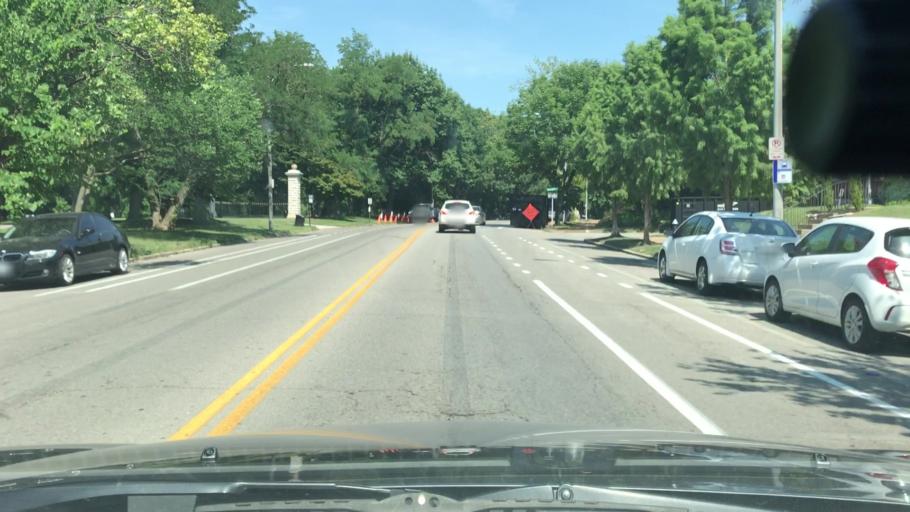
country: US
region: Missouri
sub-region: Saint Louis County
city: Richmond Heights
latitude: 38.6051
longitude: -90.2674
